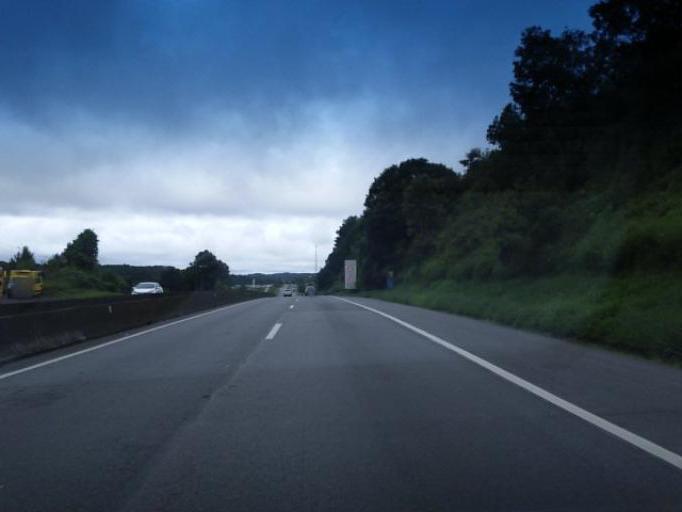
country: BR
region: Parana
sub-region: Campina Grande Do Sul
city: Campina Grande do Sul
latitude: -25.3371
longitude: -49.0365
